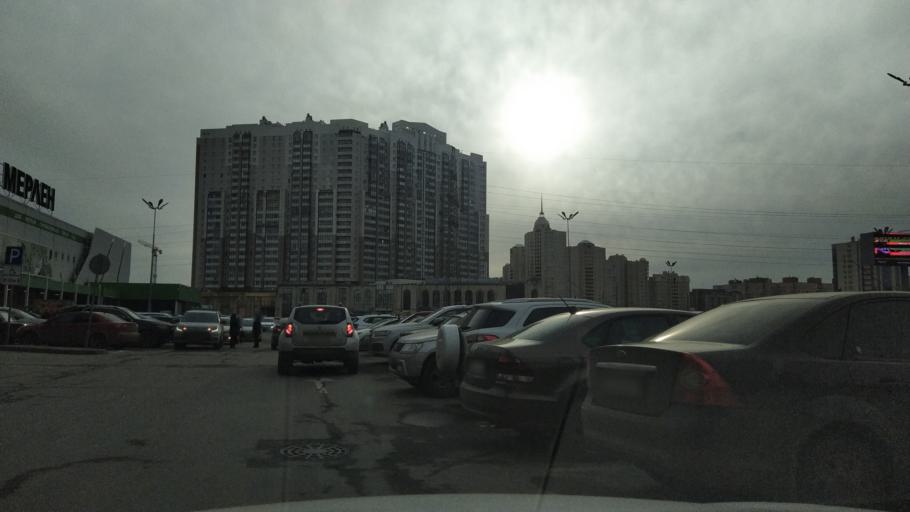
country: RU
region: Leningrad
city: Chernaya Rechka
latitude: 60.0047
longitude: 30.2998
